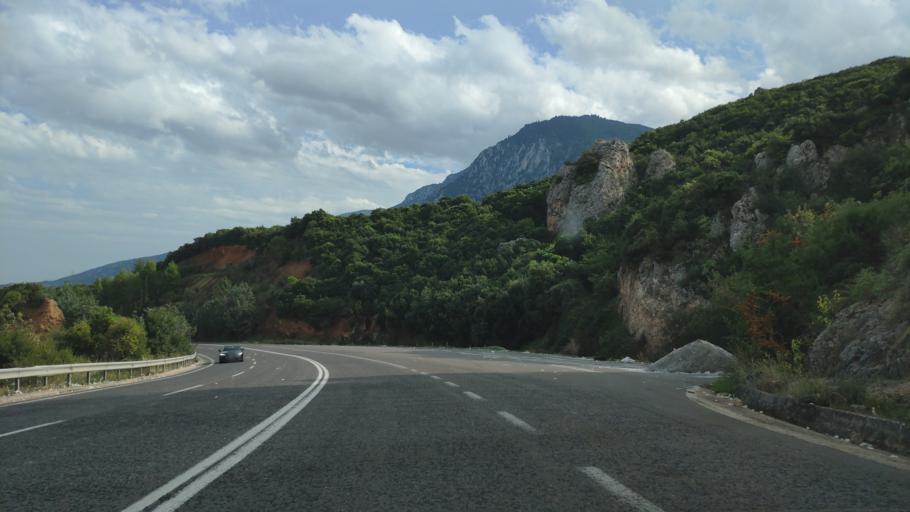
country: GR
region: Central Greece
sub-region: Nomos Fthiotidos
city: Anthili
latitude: 38.8013
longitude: 22.4972
